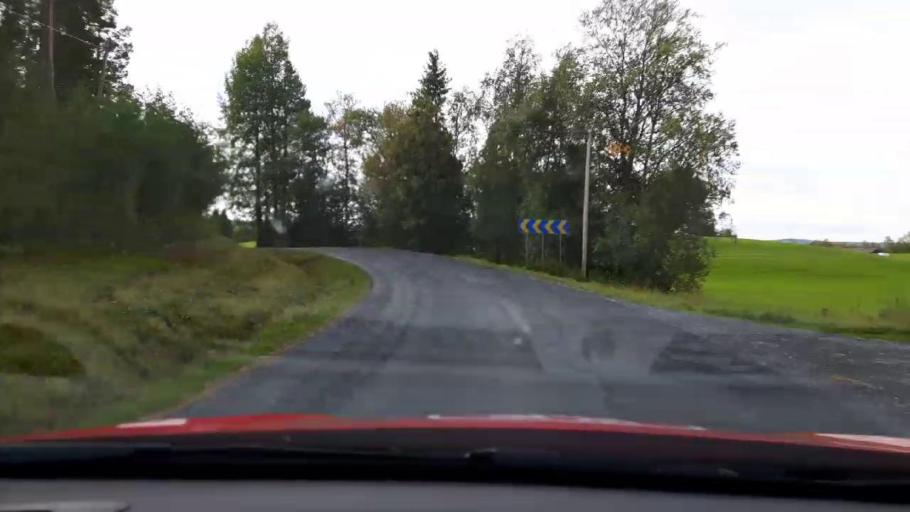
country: SE
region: Jaemtland
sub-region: Krokoms Kommun
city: Valla
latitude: 63.2702
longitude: 13.8555
